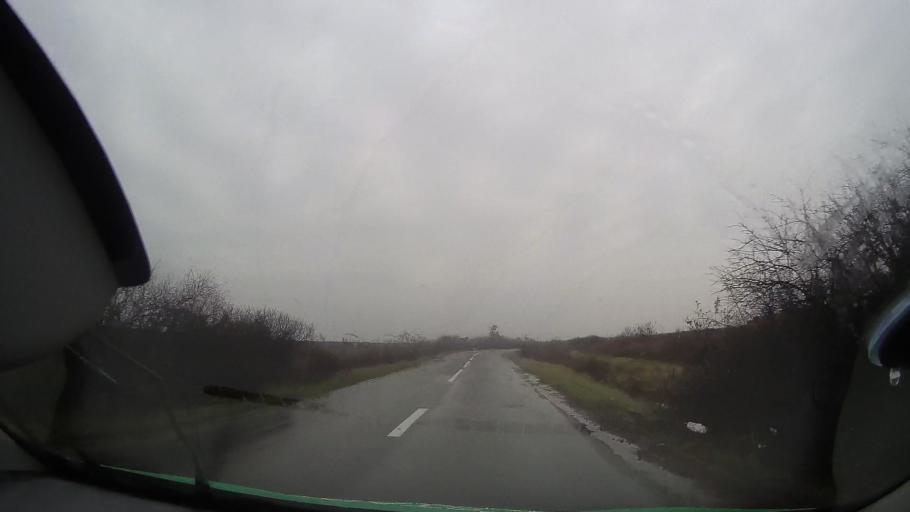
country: RO
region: Bihor
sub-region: Comuna Tinca
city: Gurbediu
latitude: 46.7905
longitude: 21.8475
